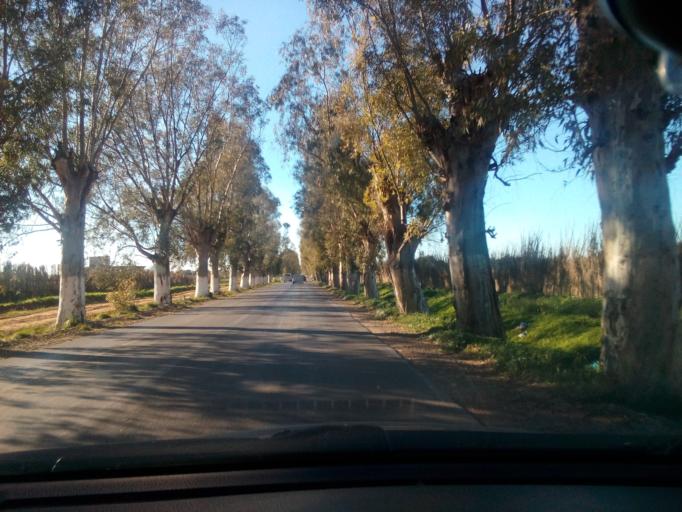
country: DZ
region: Mostaganem
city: Mostaganem
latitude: 35.9043
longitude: 0.2070
